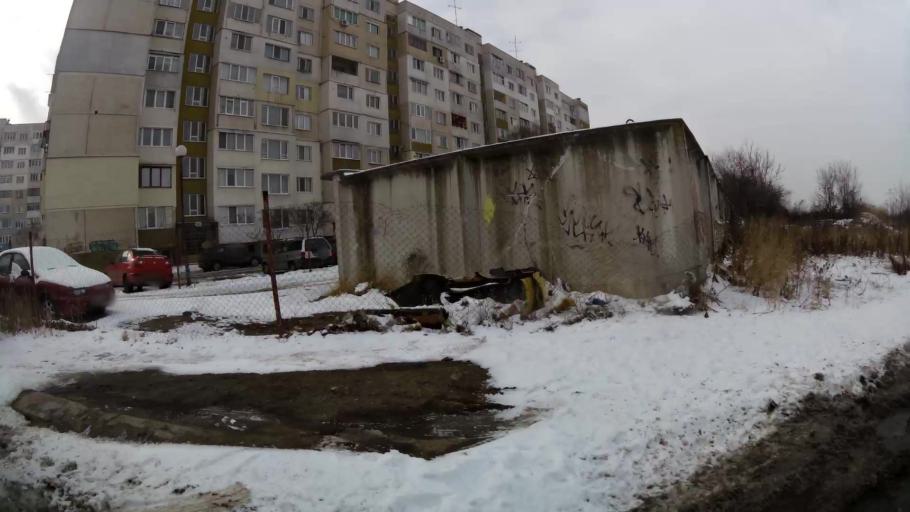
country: BG
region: Sofia-Capital
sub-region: Stolichna Obshtina
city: Sofia
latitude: 42.7141
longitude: 23.3886
